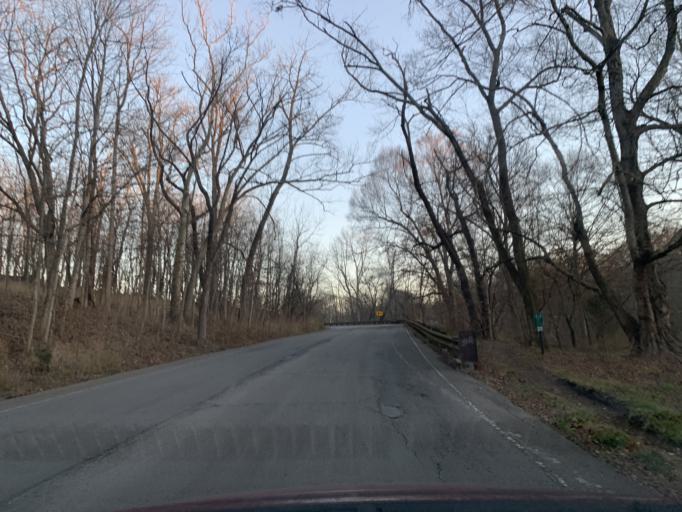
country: US
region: Kentucky
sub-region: Jefferson County
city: Saint Matthews
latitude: 38.2340
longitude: -85.6843
